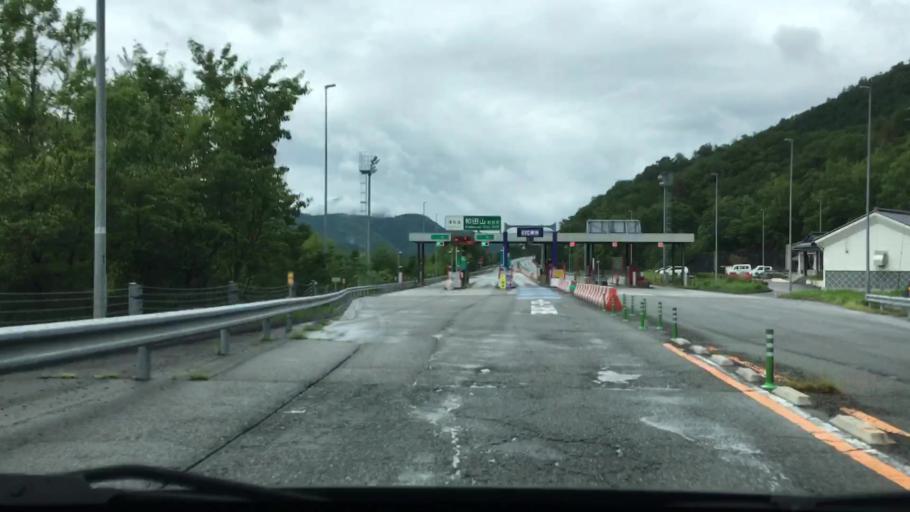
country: JP
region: Hyogo
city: Toyooka
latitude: 35.2872
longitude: 134.8225
